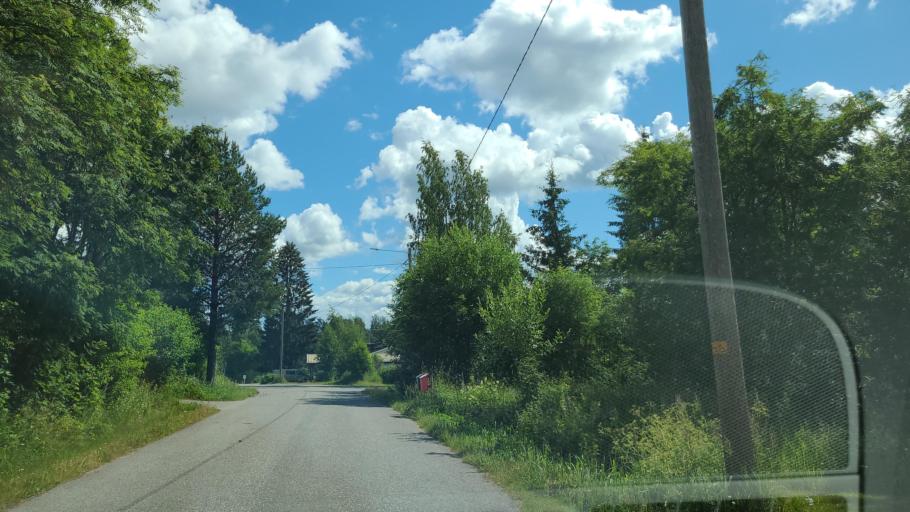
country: FI
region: Northern Savo
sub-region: Koillis-Savo
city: Kaavi
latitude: 62.9723
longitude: 28.4812
